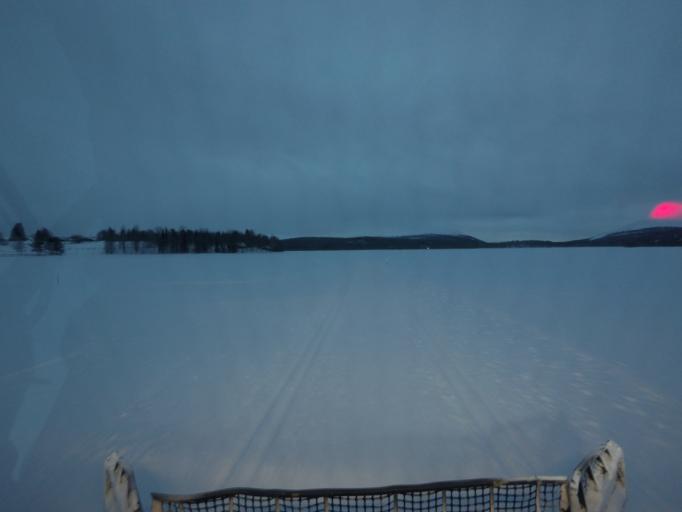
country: FI
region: Lapland
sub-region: Tunturi-Lappi
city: Kolari
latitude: 67.6115
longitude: 24.1494
